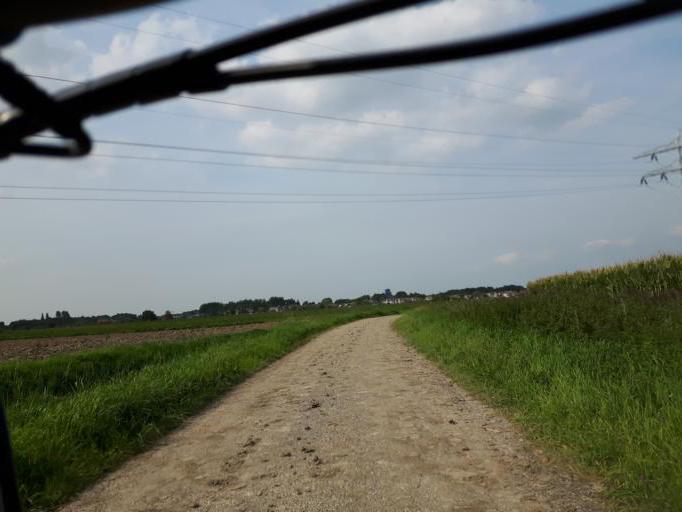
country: NL
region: Zeeland
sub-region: Gemeente Goes
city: Goes
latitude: 51.4939
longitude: 3.8639
